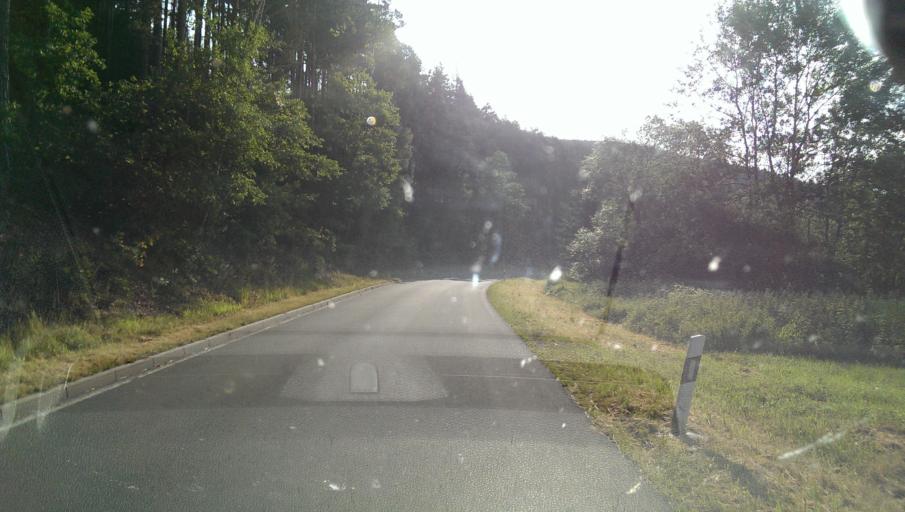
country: DE
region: Thuringia
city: Rottenbach
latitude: 50.7088
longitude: 11.1770
